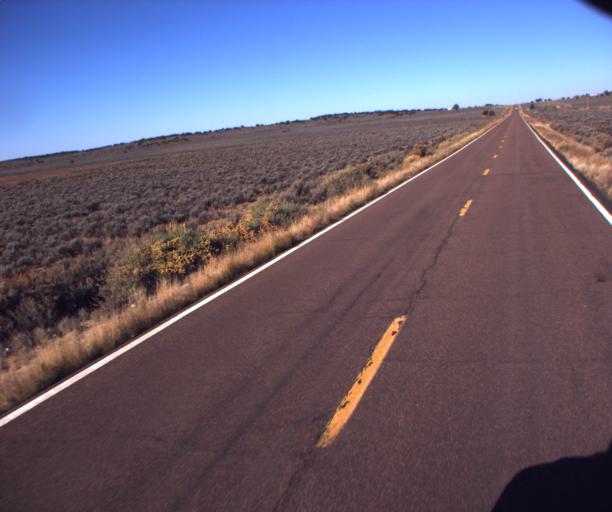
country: US
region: Arizona
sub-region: Apache County
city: Ganado
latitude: 35.7543
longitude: -109.9501
